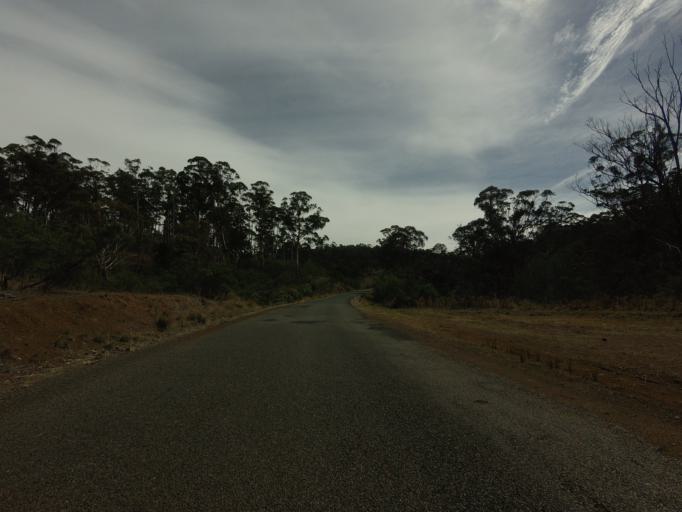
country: AU
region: Tasmania
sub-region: Sorell
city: Sorell
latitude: -42.5666
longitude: 147.6823
